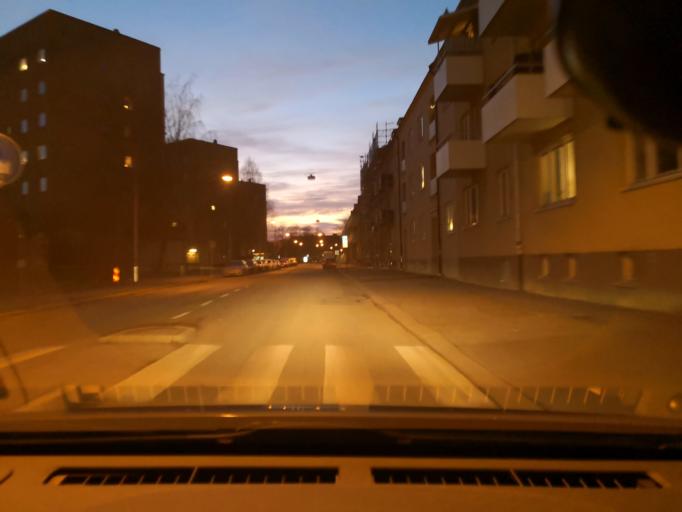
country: SE
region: OErebro
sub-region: Orebro Kommun
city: Orebro
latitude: 59.2833
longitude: 15.2292
